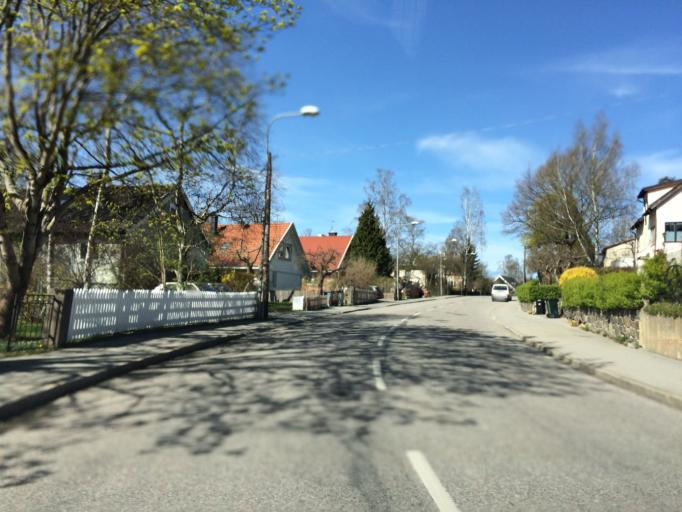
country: SE
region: Stockholm
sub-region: Huddinge Kommun
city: Huddinge
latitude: 59.2697
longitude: 17.9697
